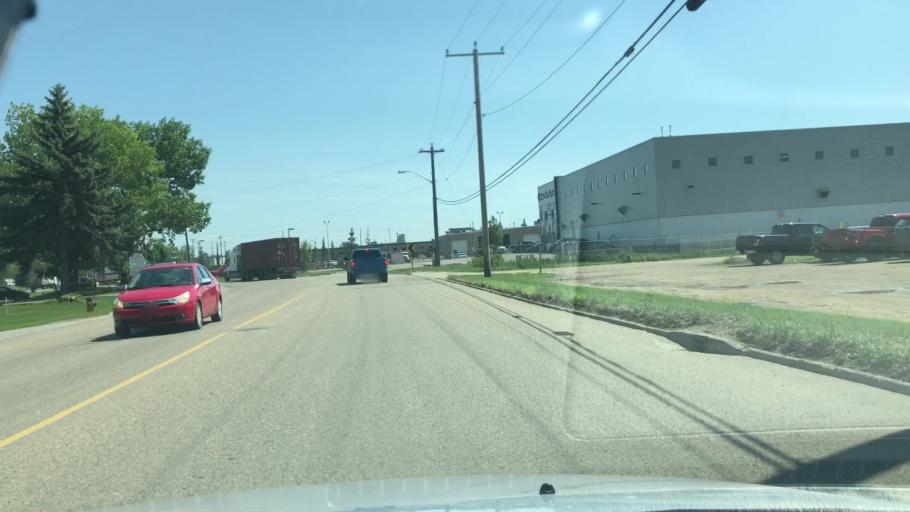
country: CA
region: Alberta
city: St. Albert
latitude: 53.5849
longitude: -113.5826
